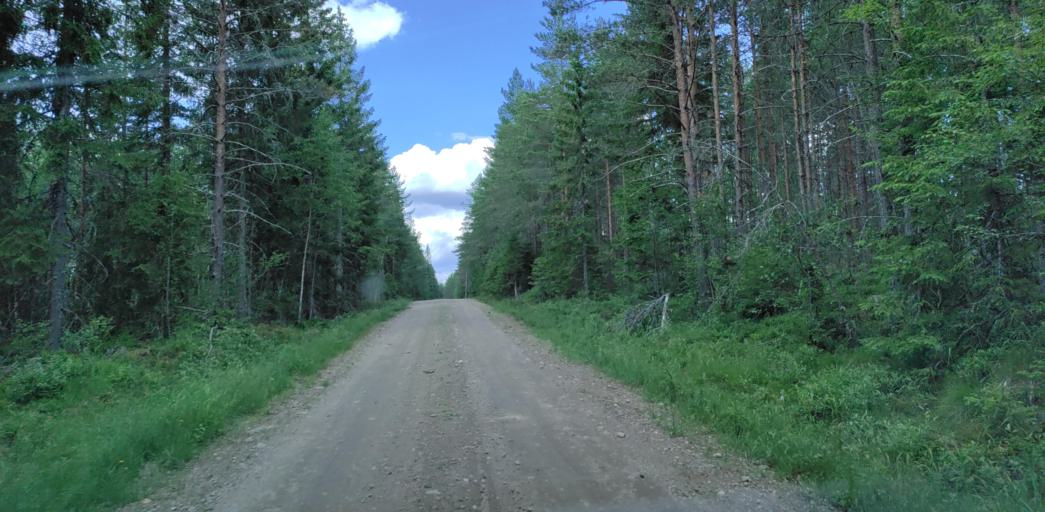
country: SE
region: Vaermland
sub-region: Hagfors Kommun
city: Ekshaerad
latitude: 60.0803
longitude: 13.3465
